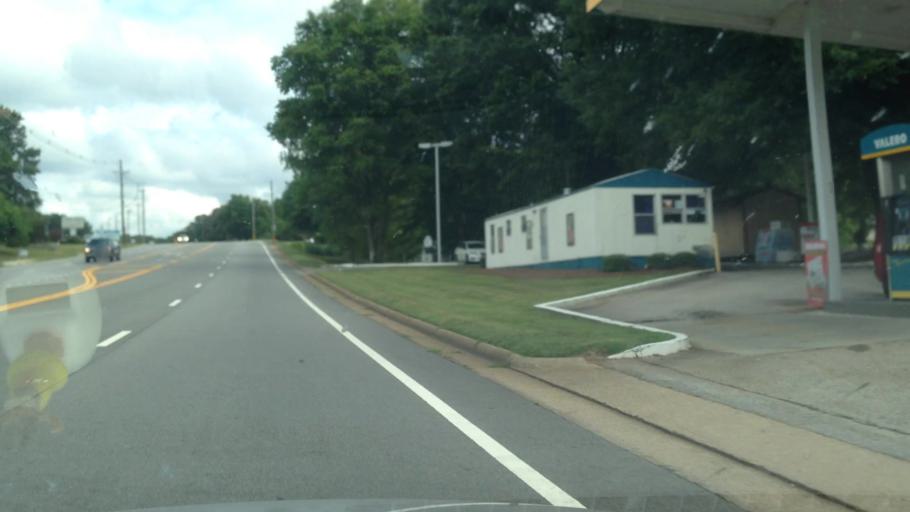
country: US
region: Virginia
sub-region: Pittsylvania County
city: Mount Hermon
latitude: 36.6646
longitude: -79.3746
